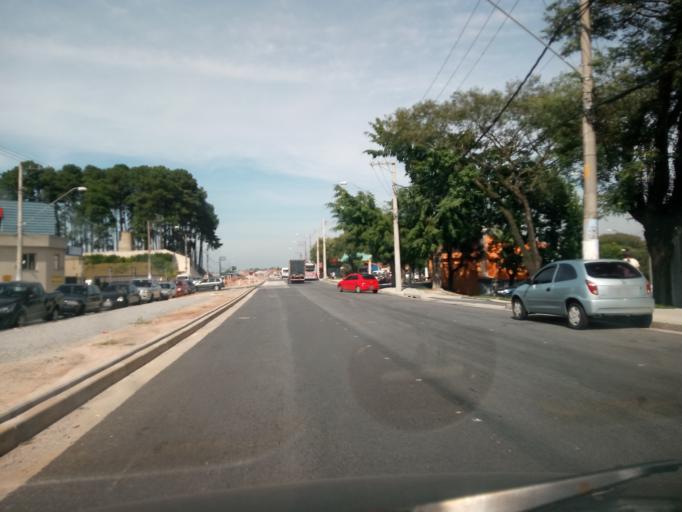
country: BR
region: Sao Paulo
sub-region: Sao Bernardo Do Campo
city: Sao Bernardo do Campo
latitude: -23.7320
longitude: -46.5788
